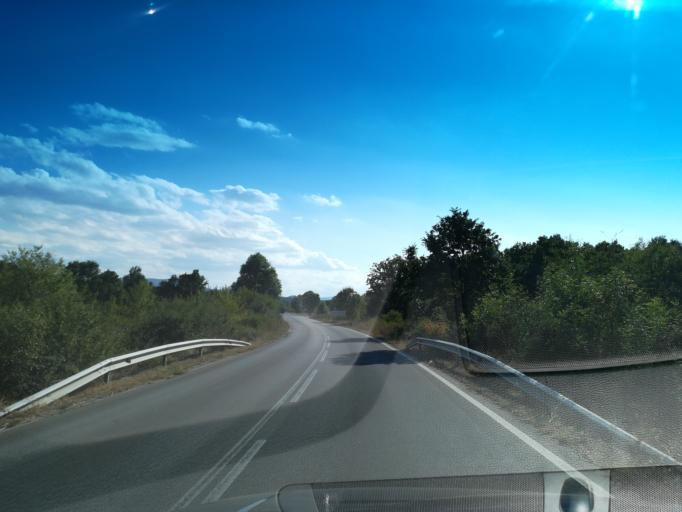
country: BG
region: Khaskovo
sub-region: Obshtina Mineralni Bani
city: Mineralni Bani
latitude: 41.9894
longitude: 25.3553
